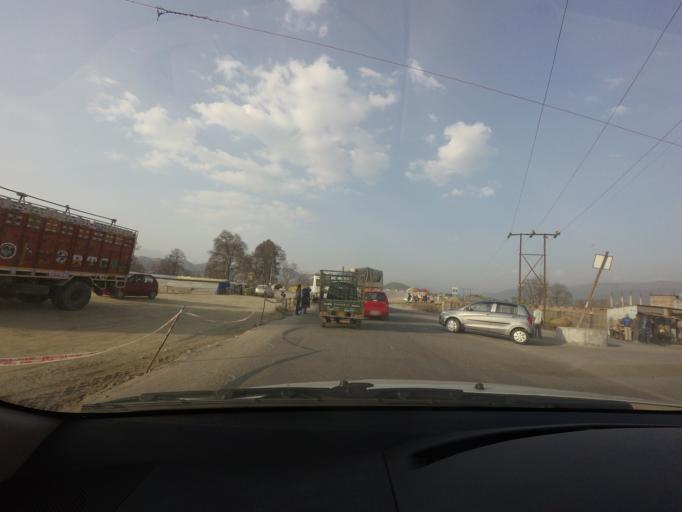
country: IN
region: Himachal Pradesh
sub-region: Mandi
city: Sundarnagar
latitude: 31.5963
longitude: 76.9243
